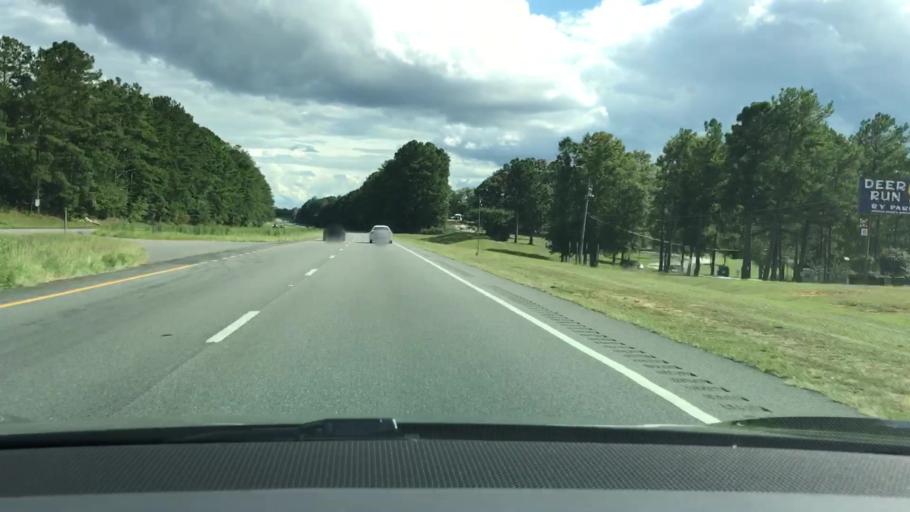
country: US
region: Alabama
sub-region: Pike County
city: Troy
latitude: 31.8964
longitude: -86.0103
